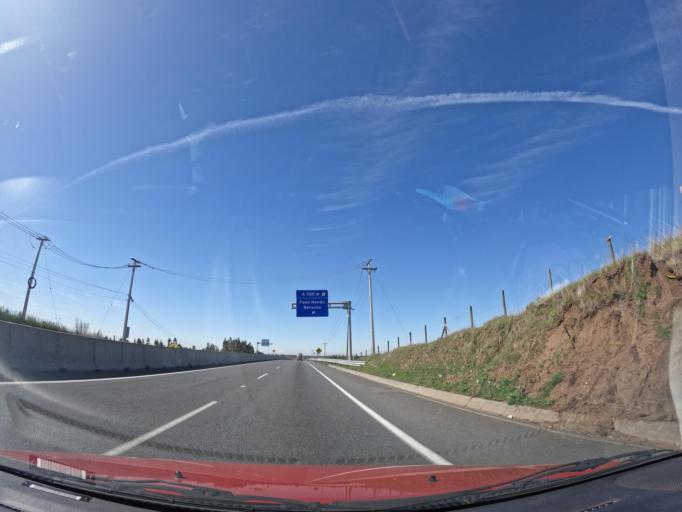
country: CL
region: Biobio
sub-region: Provincia de Biobio
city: Yumbel
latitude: -37.0009
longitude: -72.5507
